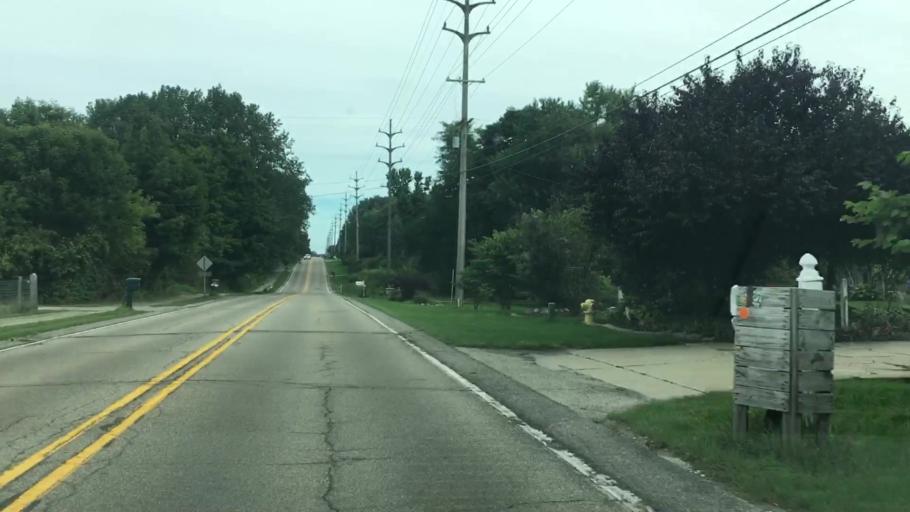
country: US
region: Michigan
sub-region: Ottawa County
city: Jenison
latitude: 42.8648
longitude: -85.7822
